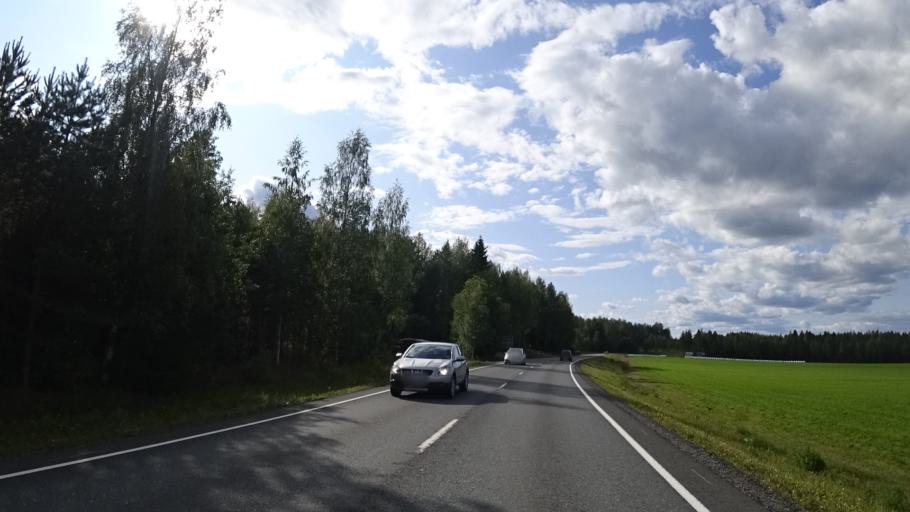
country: FI
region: North Karelia
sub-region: Keski-Karjala
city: Tohmajaervi
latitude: 62.1901
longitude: 30.4410
